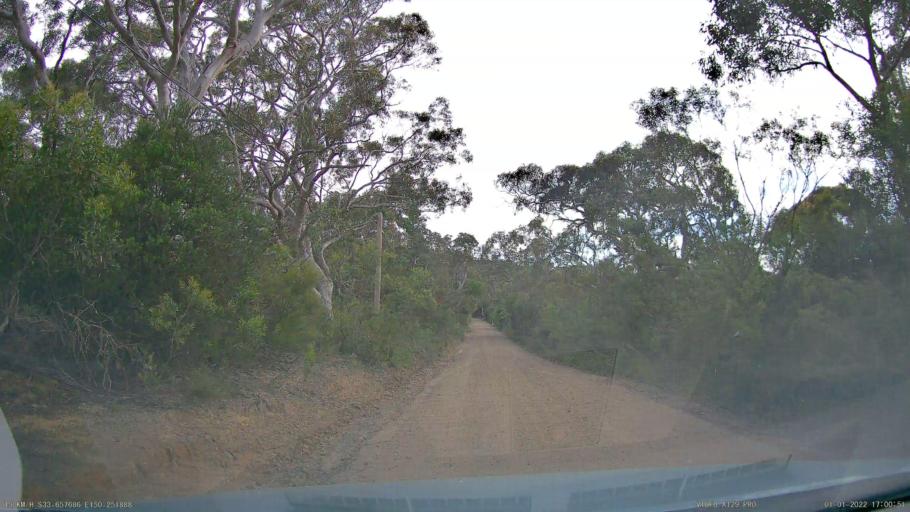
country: AU
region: New South Wales
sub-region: Blue Mountains Municipality
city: Blackheath
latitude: -33.6577
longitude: 150.2519
